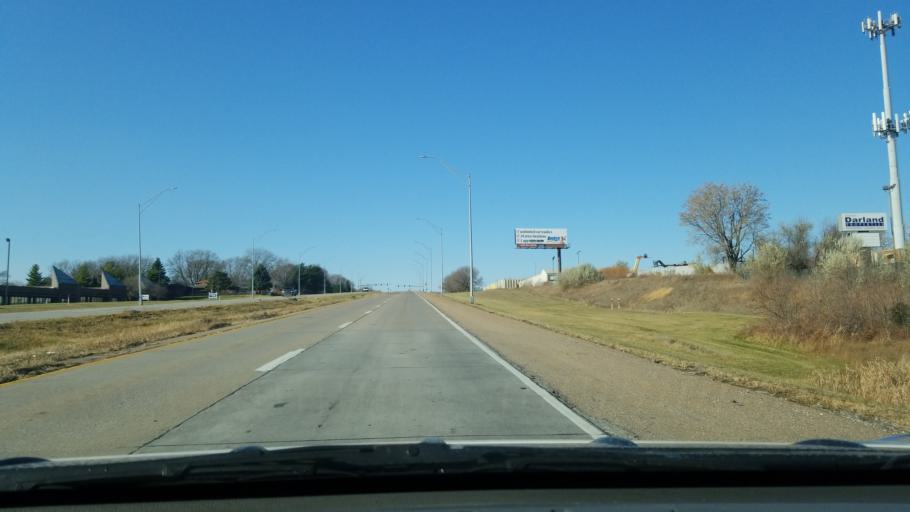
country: US
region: Nebraska
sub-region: Douglas County
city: Ralston
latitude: 41.2126
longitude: -96.0658
